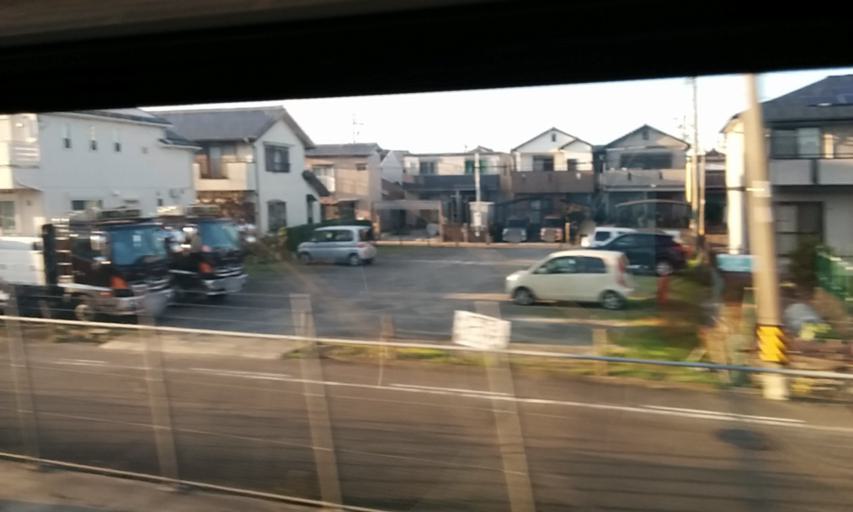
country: JP
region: Aichi
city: Kasugai
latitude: 35.2402
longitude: 136.9775
